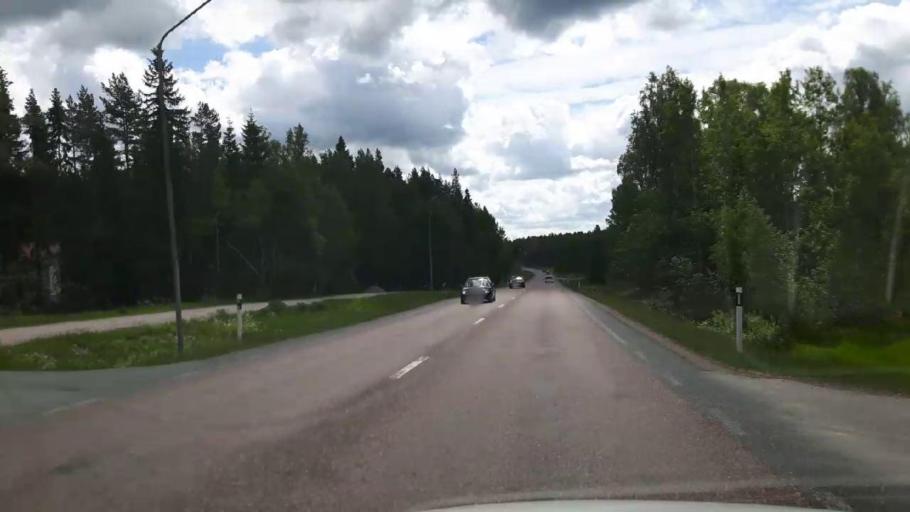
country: SE
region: Dalarna
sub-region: Faluns Kommun
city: Falun
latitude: 60.5125
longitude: 15.7365
